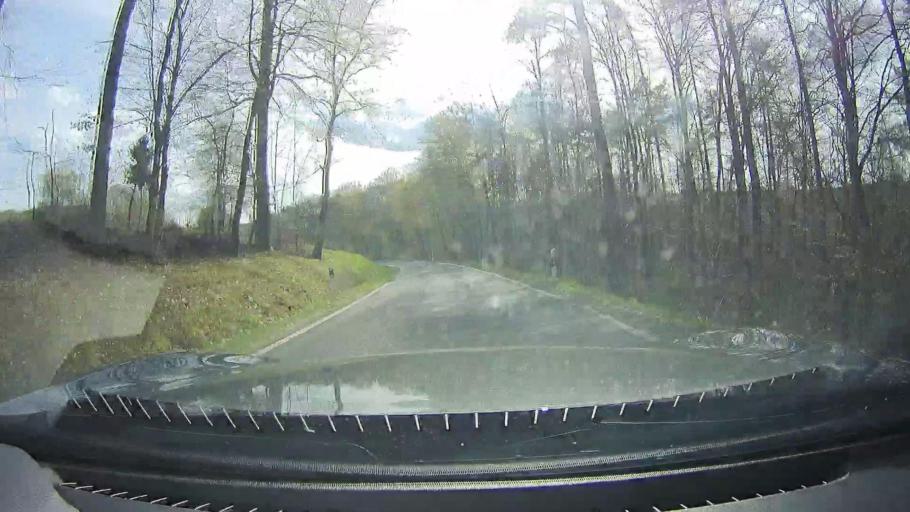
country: DE
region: Bavaria
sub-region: Regierungsbezirk Unterfranken
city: Weilbach
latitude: 49.6233
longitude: 9.2561
